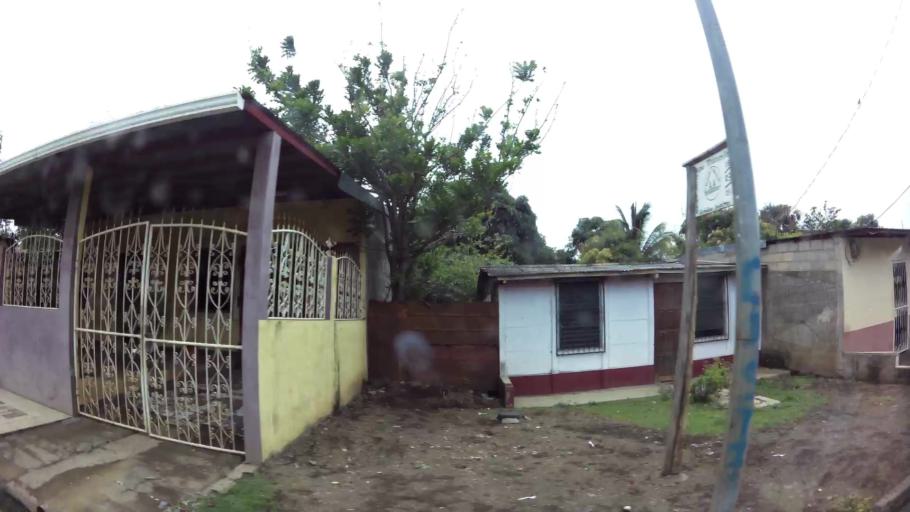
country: NI
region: Granada
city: Nandaime
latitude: 11.7594
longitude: -86.0591
